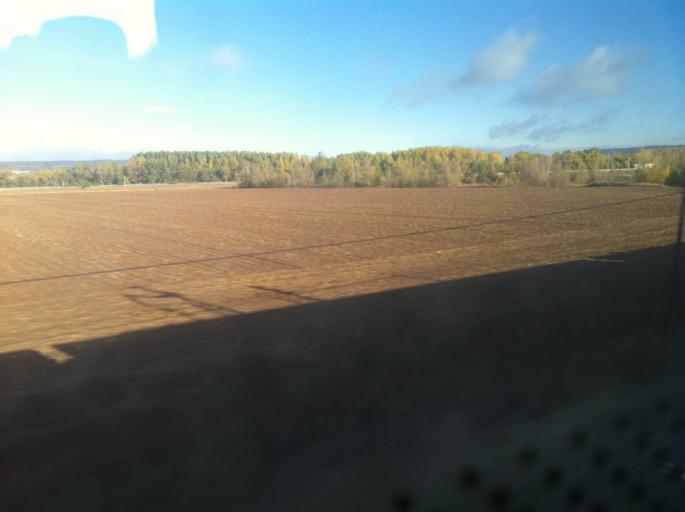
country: ES
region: Castille and Leon
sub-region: Provincia de Palencia
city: Cordovilla la Real
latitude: 42.0367
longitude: -4.2665
